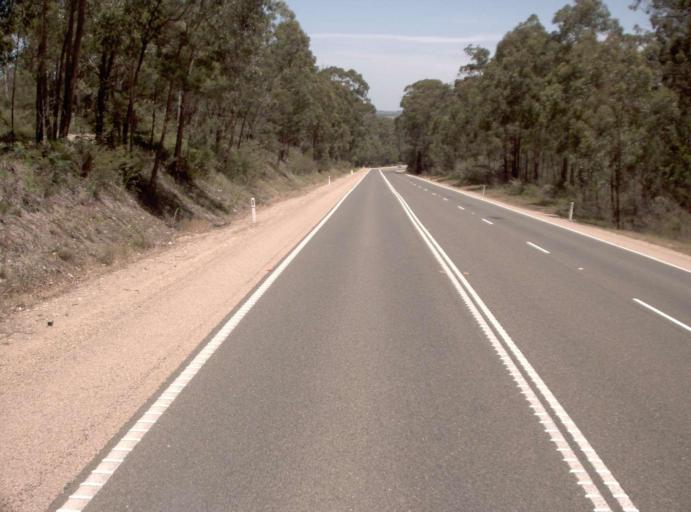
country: AU
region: Victoria
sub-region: East Gippsland
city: Bairnsdale
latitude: -37.7415
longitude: 147.7646
